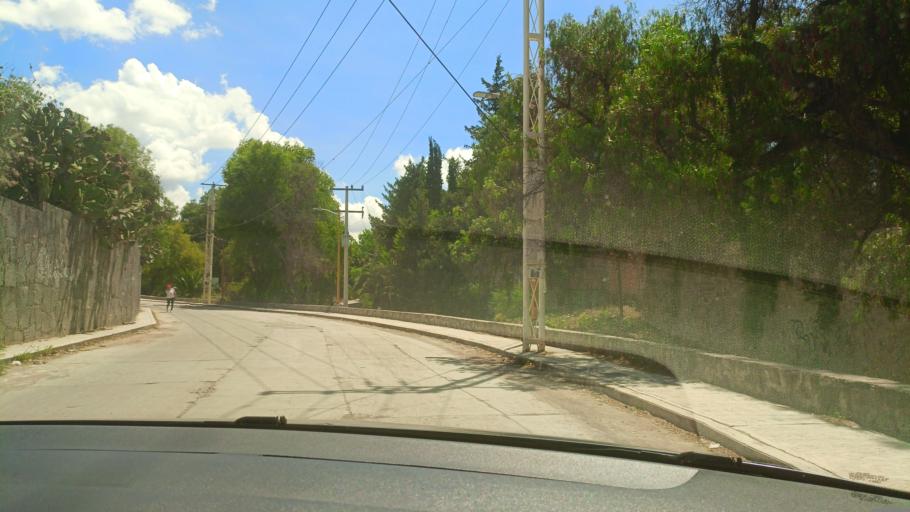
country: MX
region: Guanajuato
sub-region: San Luis de la Paz
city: San Luis de la Paz
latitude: 21.3003
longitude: -100.5058
